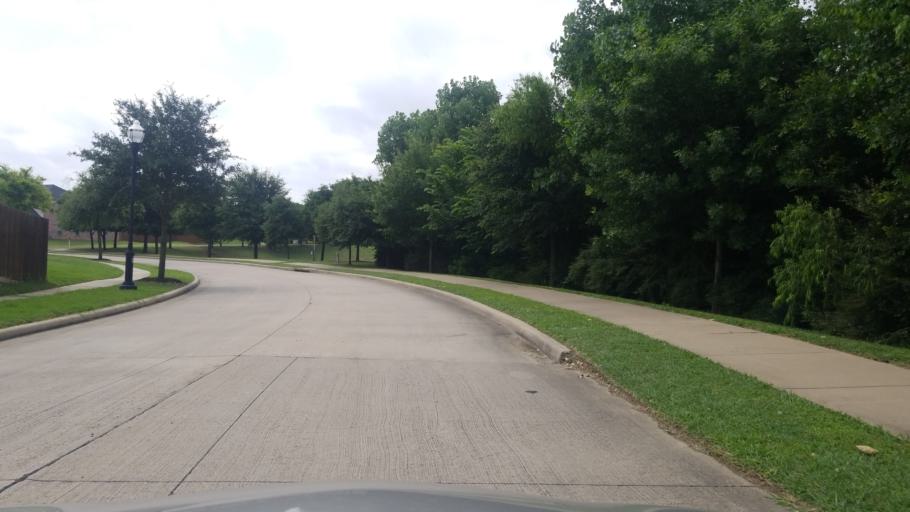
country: US
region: Texas
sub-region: Dallas County
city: Duncanville
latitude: 32.6851
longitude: -96.9382
